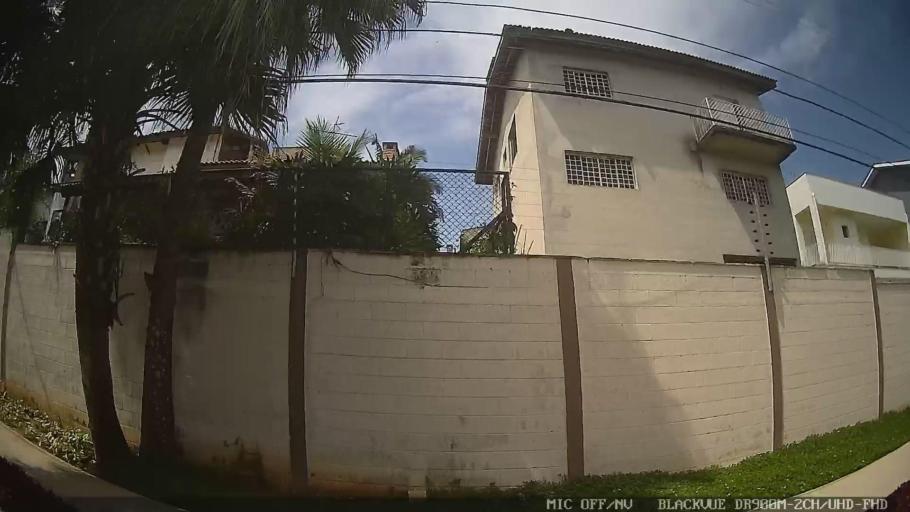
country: BR
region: Sao Paulo
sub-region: Mogi das Cruzes
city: Mogi das Cruzes
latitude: -23.4666
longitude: -46.2557
